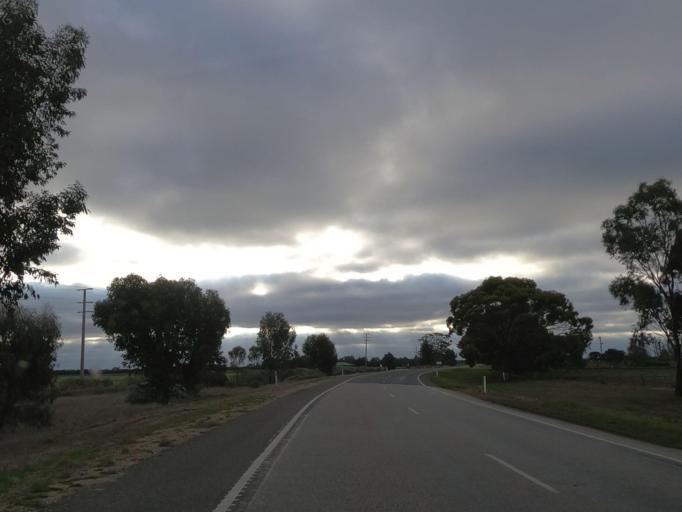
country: AU
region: Victoria
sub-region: Swan Hill
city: Swan Hill
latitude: -35.7290
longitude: 143.8924
